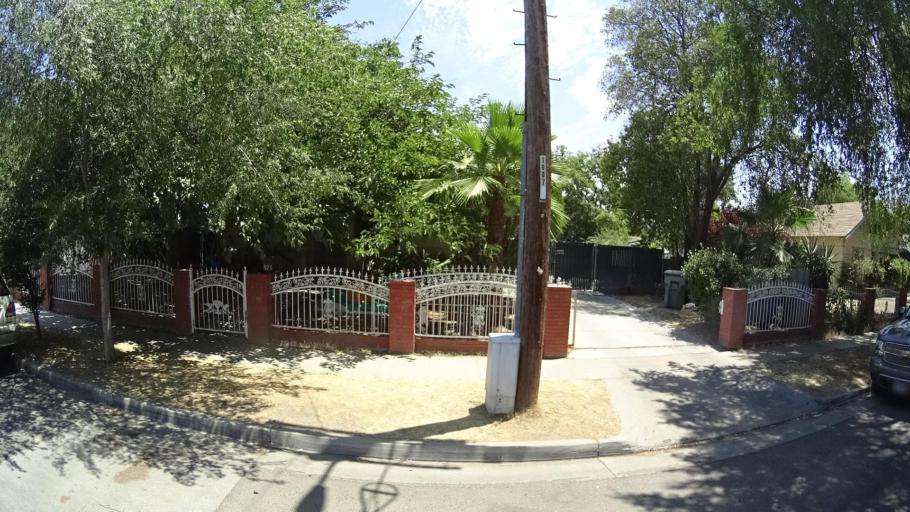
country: US
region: California
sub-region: Fresno County
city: Fresno
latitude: 36.7342
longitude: -119.7611
